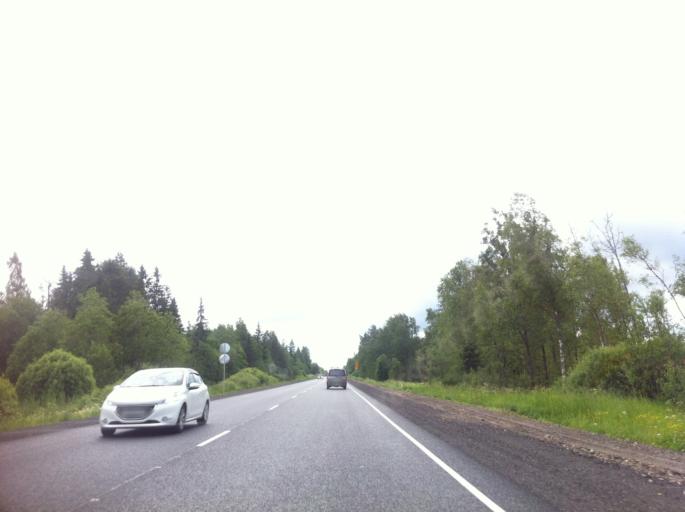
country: RU
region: Leningrad
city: Rozhdestveno
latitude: 59.2376
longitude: 29.9293
